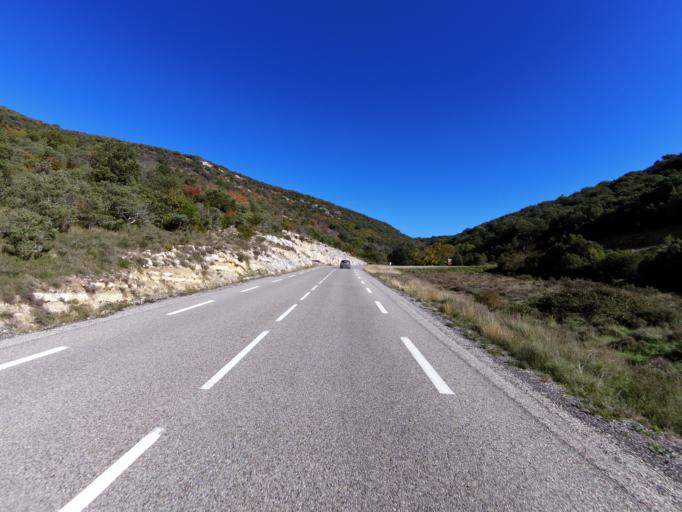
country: FR
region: Rhone-Alpes
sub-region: Departement de l'Ardeche
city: Ruoms
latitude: 44.4061
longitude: 4.4537
